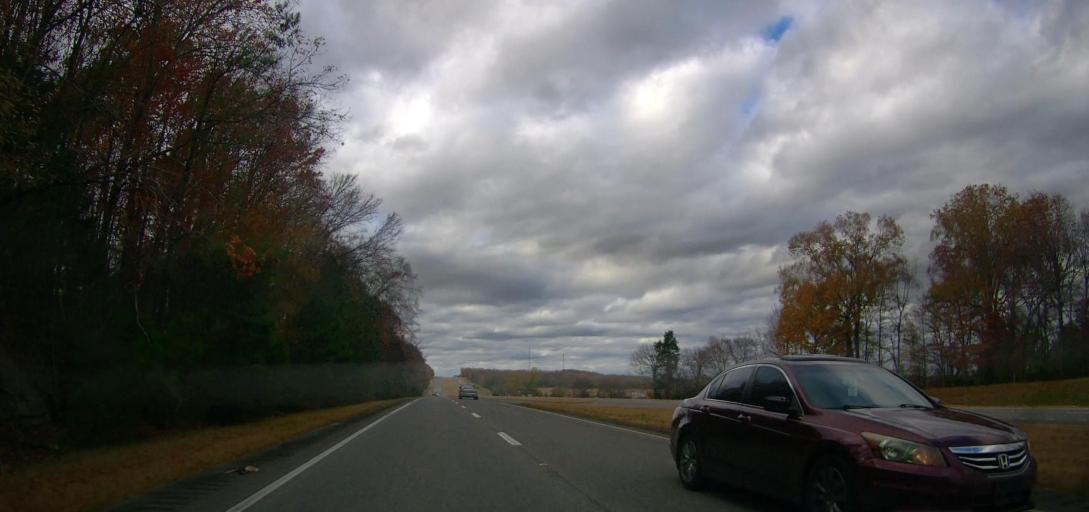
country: US
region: Alabama
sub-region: Morgan County
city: Danville
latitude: 34.3907
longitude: -87.1142
